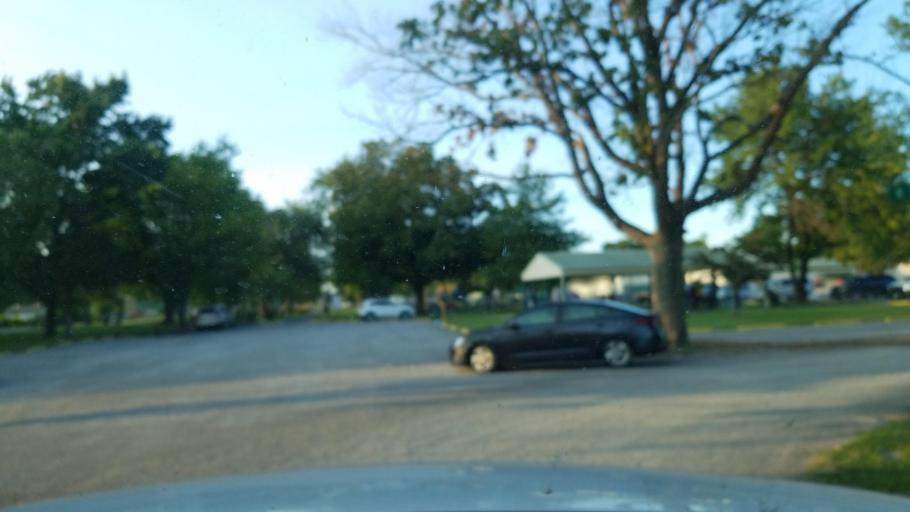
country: US
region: Illinois
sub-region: Saline County
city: Harrisburg
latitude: 37.7351
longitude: -88.5547
